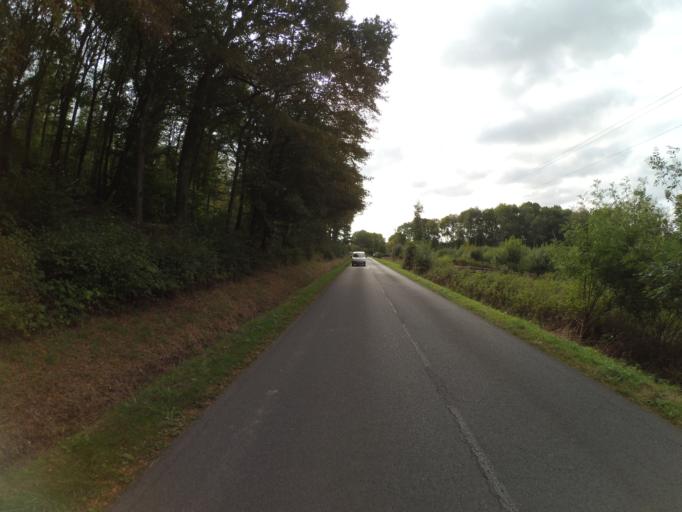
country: FR
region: Centre
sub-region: Departement d'Indre-et-Loire
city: Reugny
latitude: 47.4813
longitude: 0.8924
